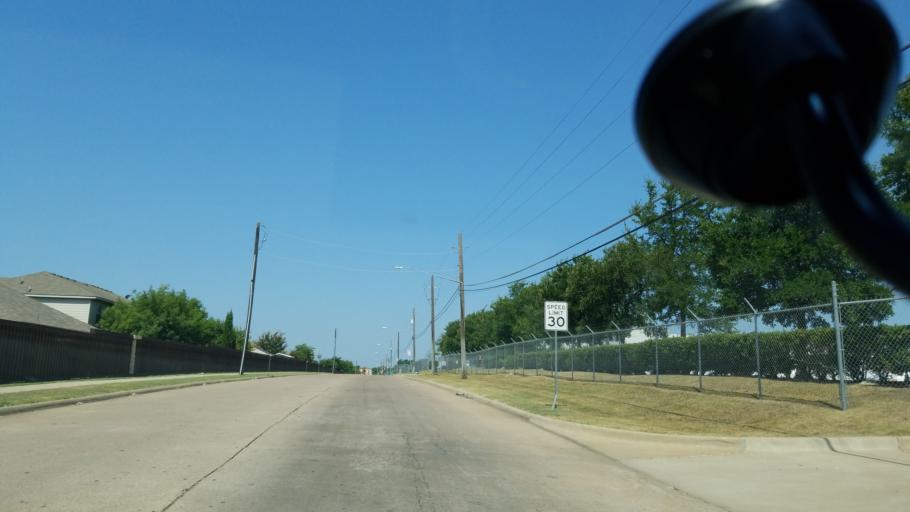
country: US
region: Texas
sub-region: Dallas County
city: Cockrell Hill
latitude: 32.7134
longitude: -96.8662
